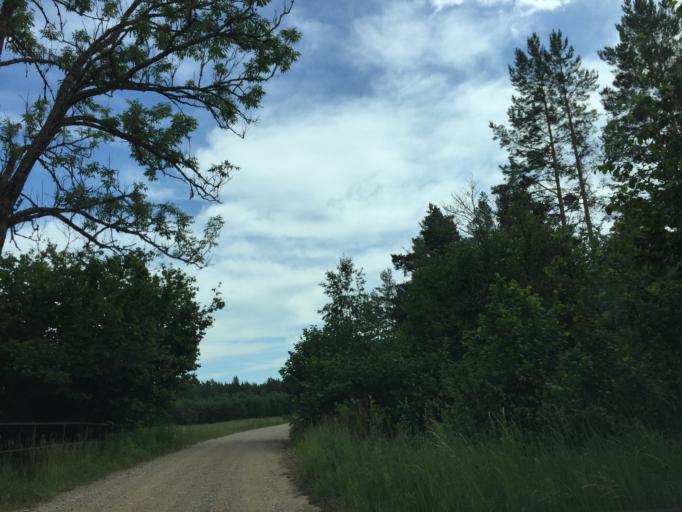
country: LV
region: Engure
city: Smarde
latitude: 57.0519
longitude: 23.2887
